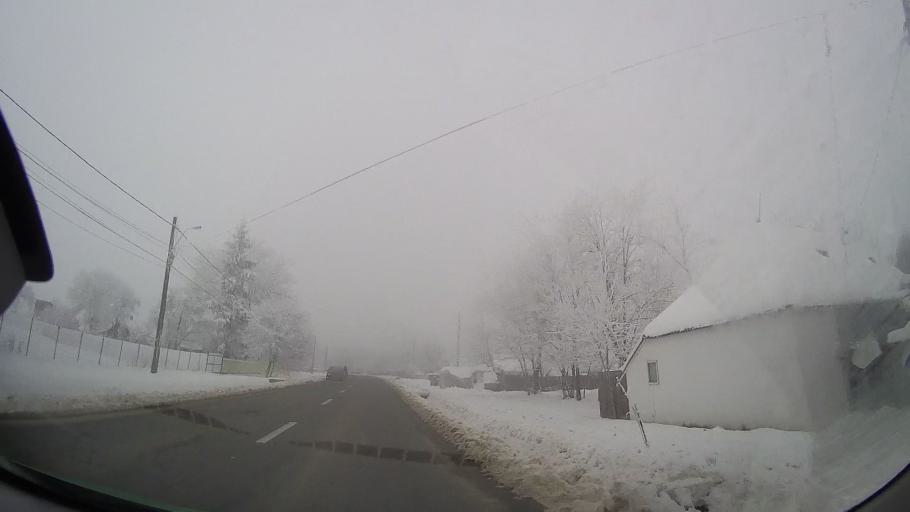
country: RO
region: Iasi
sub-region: Comuna Mogosesti-Siret
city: Mogosesti-Siret
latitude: 47.1636
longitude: 26.7710
